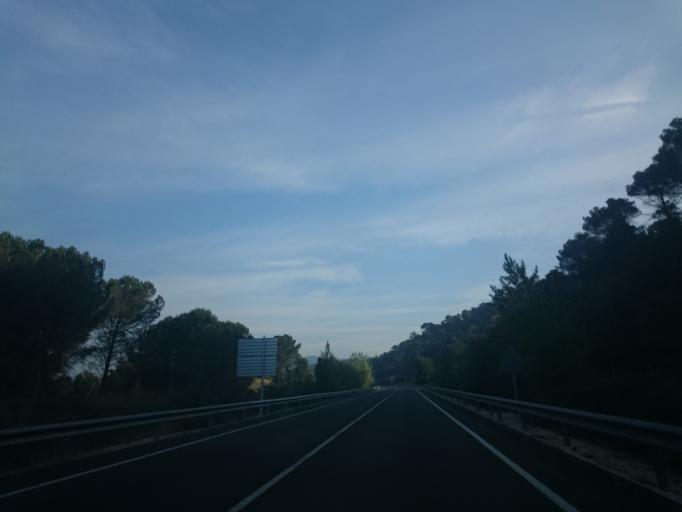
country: ES
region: Catalonia
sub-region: Provincia de Barcelona
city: La Pobla de Claramunt
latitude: 41.5463
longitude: 1.6922
